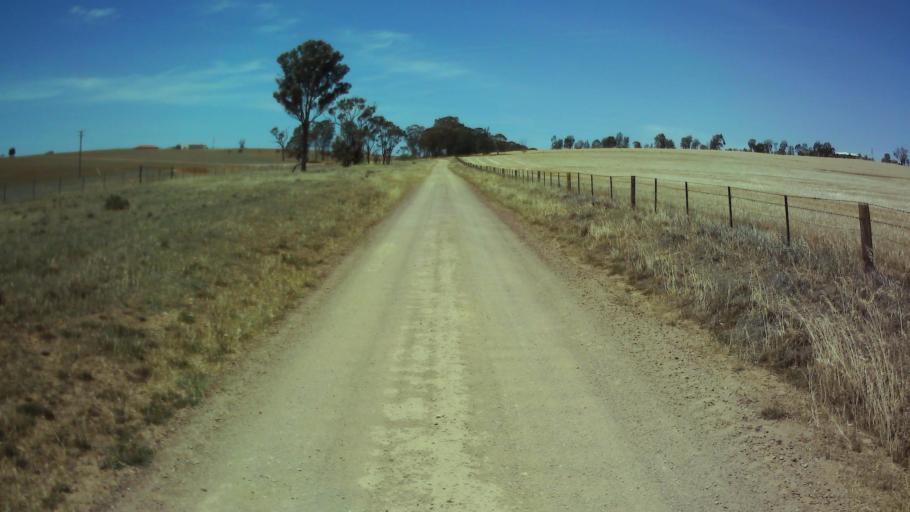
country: AU
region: New South Wales
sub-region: Weddin
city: Grenfell
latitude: -33.9292
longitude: 148.1671
